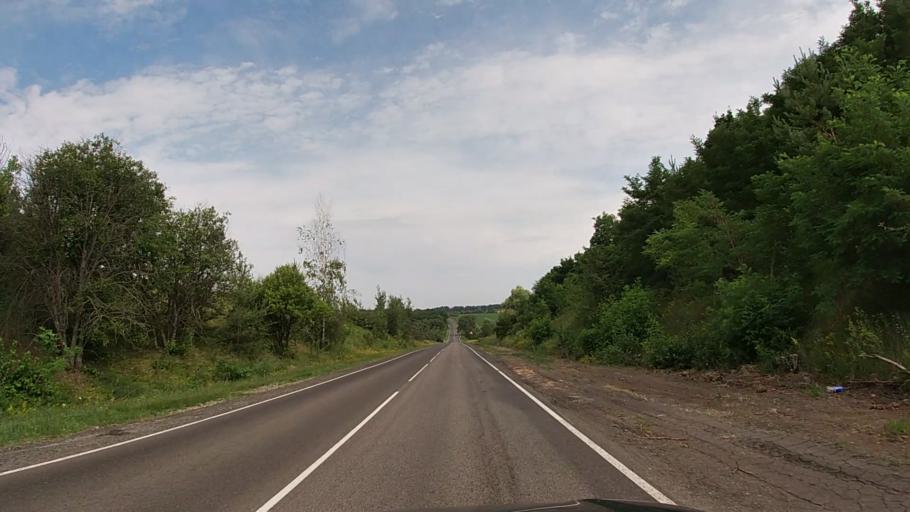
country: RU
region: Belgorod
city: Krasnaya Yaruga
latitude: 50.8241
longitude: 35.4998
